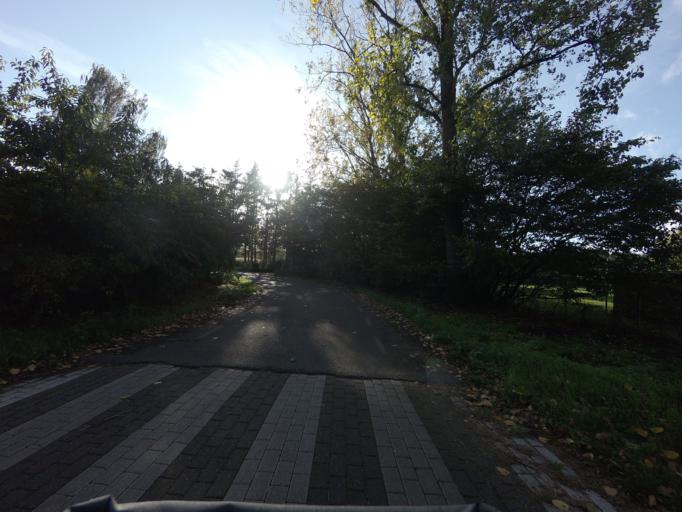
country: NL
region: North Holland
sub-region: Gemeente Bussum
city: Bussum
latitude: 52.2579
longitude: 5.1707
